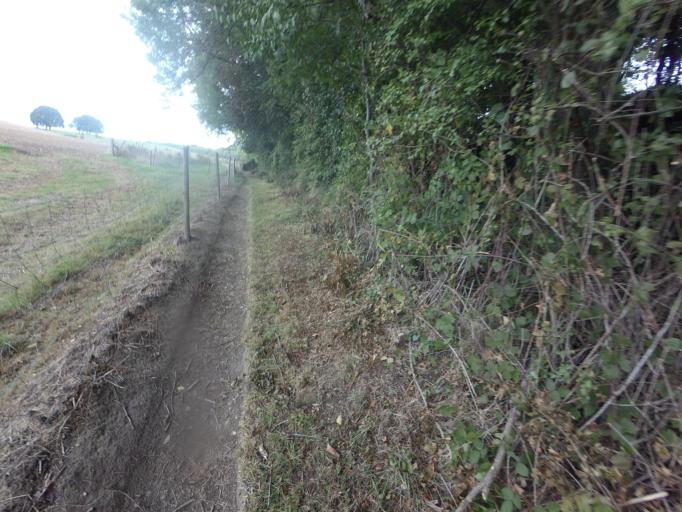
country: NL
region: Limburg
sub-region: Eijsden-Margraten
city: Margraten
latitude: 50.8068
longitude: 5.8559
